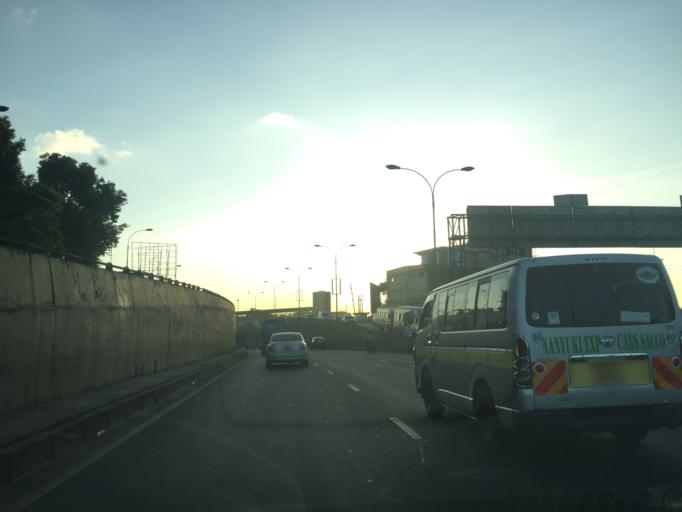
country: KE
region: Nairobi Area
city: Pumwani
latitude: -1.2649
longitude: 36.8364
